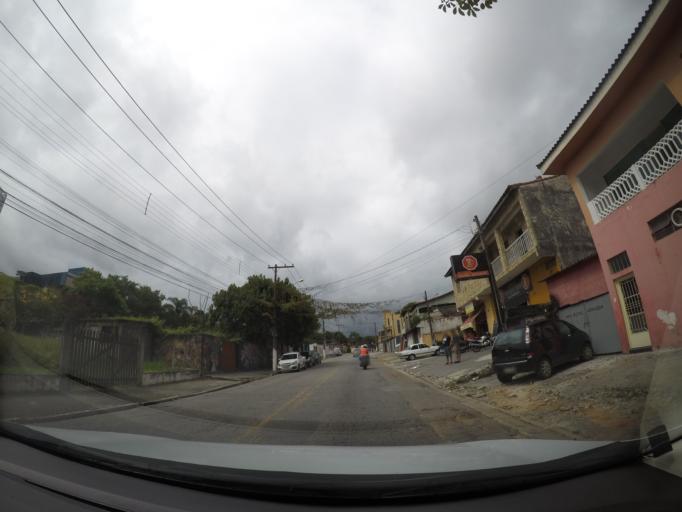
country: BR
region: Sao Paulo
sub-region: Aruja
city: Aruja
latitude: -23.3936
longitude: -46.3144
